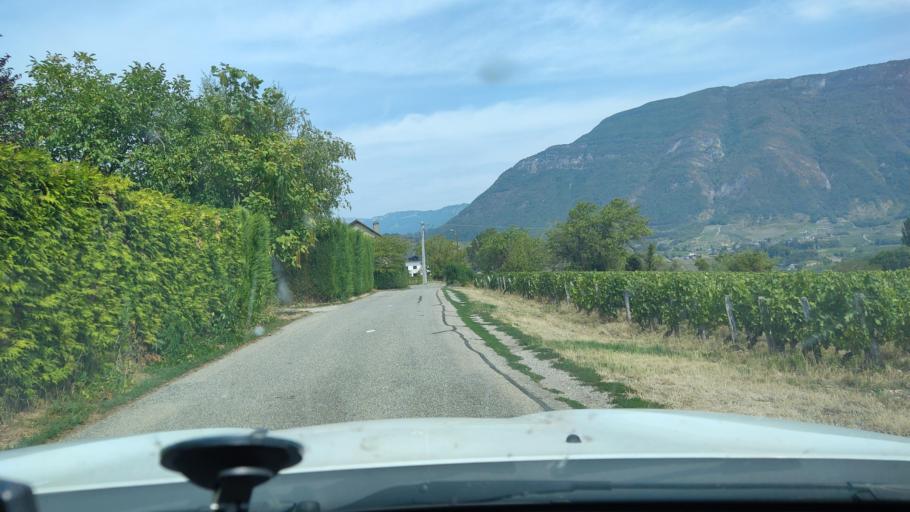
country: FR
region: Rhone-Alpes
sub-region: Departement de la Savoie
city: Les Marches
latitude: 45.5102
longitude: 5.9863
